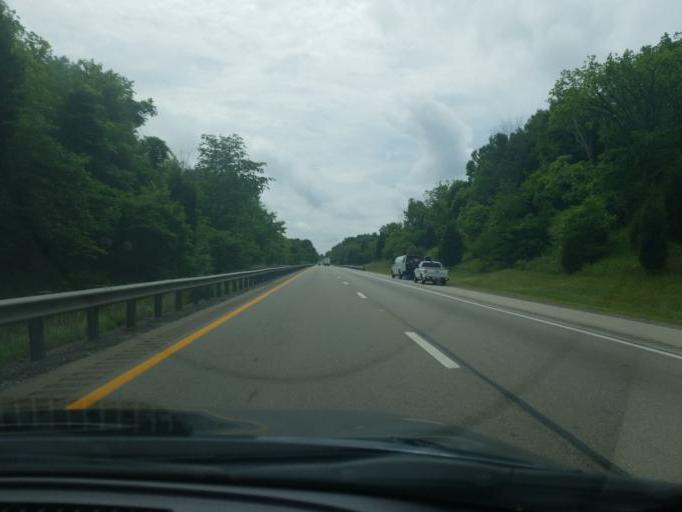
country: US
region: Indiana
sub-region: Switzerland County
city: Vevay
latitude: 38.6771
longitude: -84.9878
